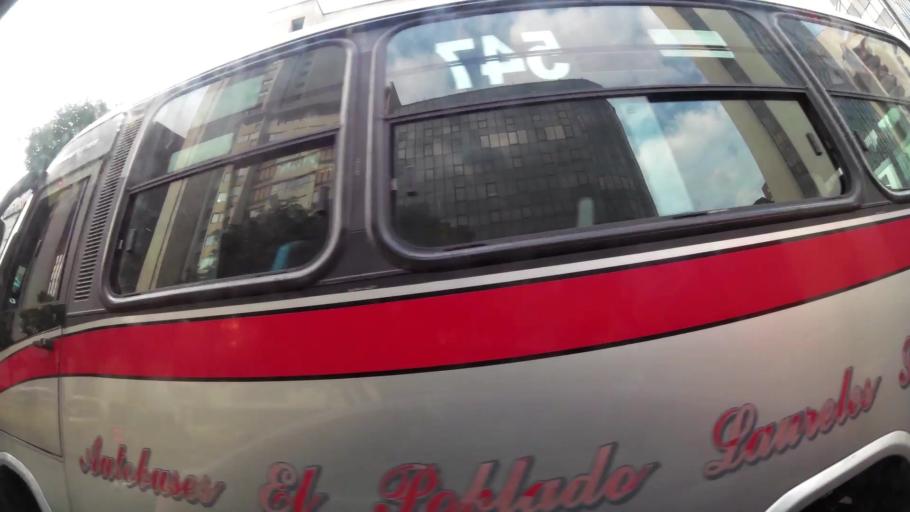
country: CO
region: Antioquia
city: Medellin
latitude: 6.2504
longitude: -75.5639
